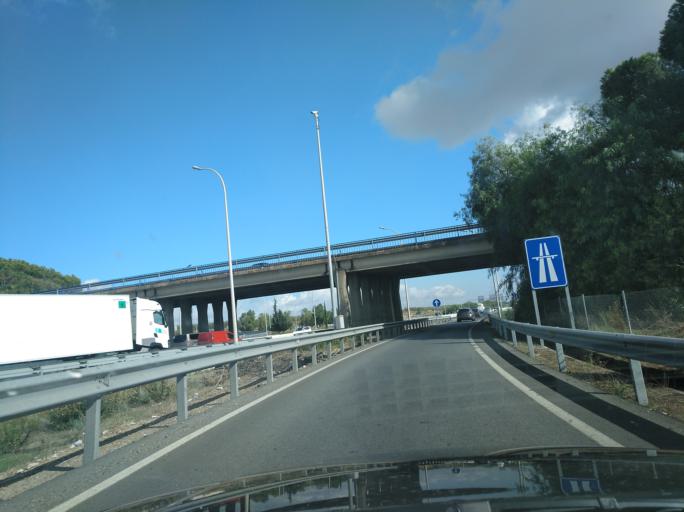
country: ES
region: Andalusia
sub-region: Provincia de Sevilla
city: Umbrete
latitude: 37.3595
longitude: -6.1421
